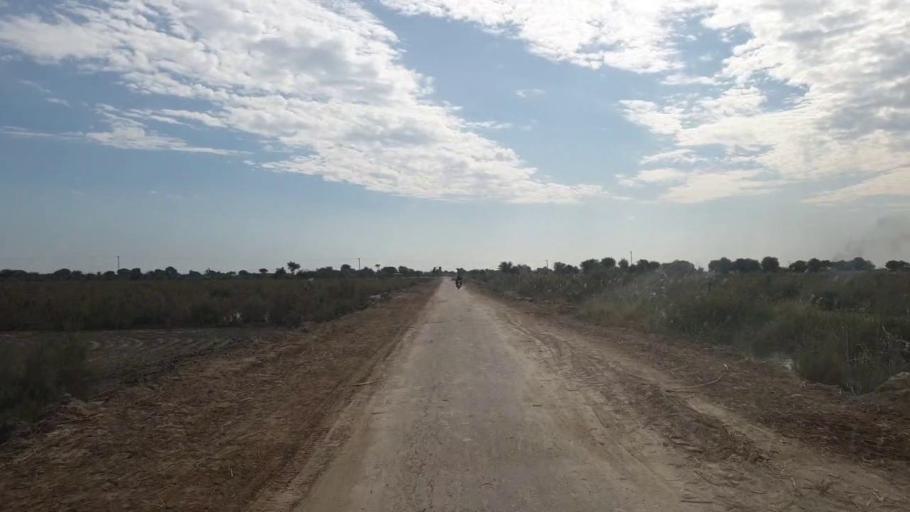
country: PK
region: Sindh
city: Jhol
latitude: 25.9980
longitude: 68.8960
